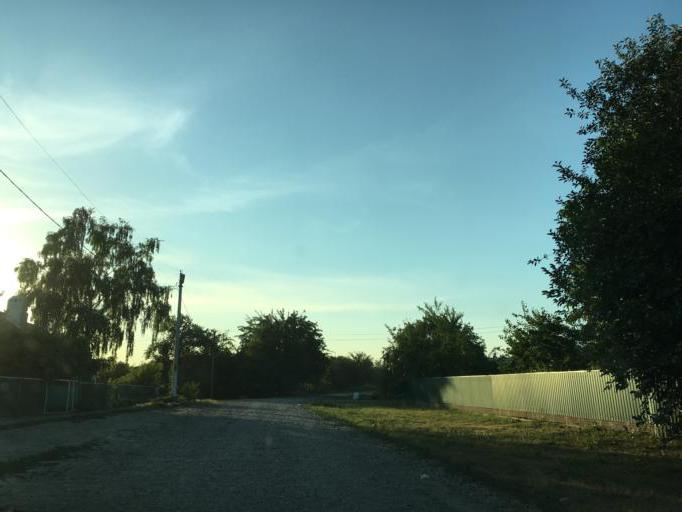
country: RU
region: Krasnodarskiy
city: Kushchevskaya
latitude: 46.5654
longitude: 39.6500
